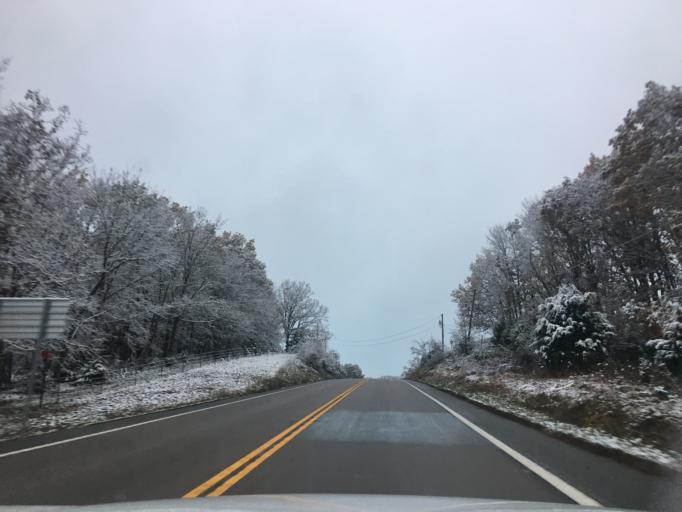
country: US
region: Missouri
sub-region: Osage County
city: Linn
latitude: 38.4731
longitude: -91.7826
